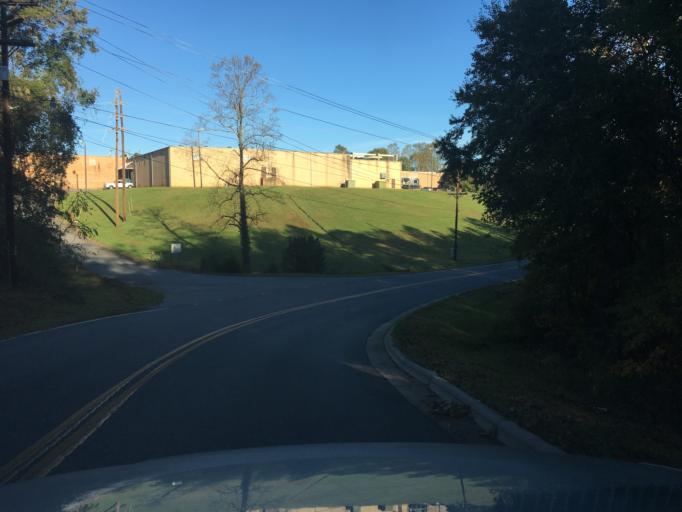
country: US
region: North Carolina
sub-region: Catawba County
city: Hickory
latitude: 35.7266
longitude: -81.3141
